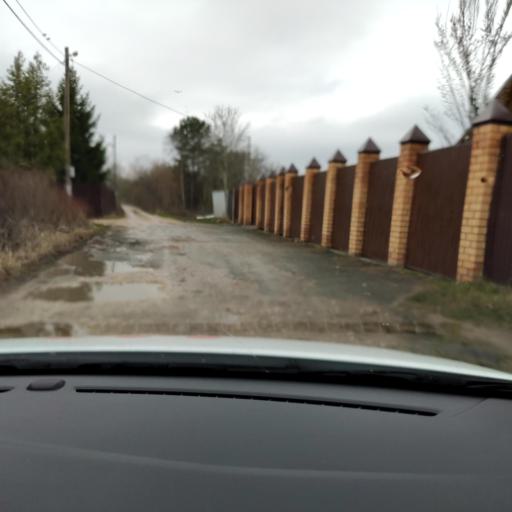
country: RU
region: Tatarstan
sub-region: Gorod Kazan'
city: Kazan
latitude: 55.6883
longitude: 49.0683
